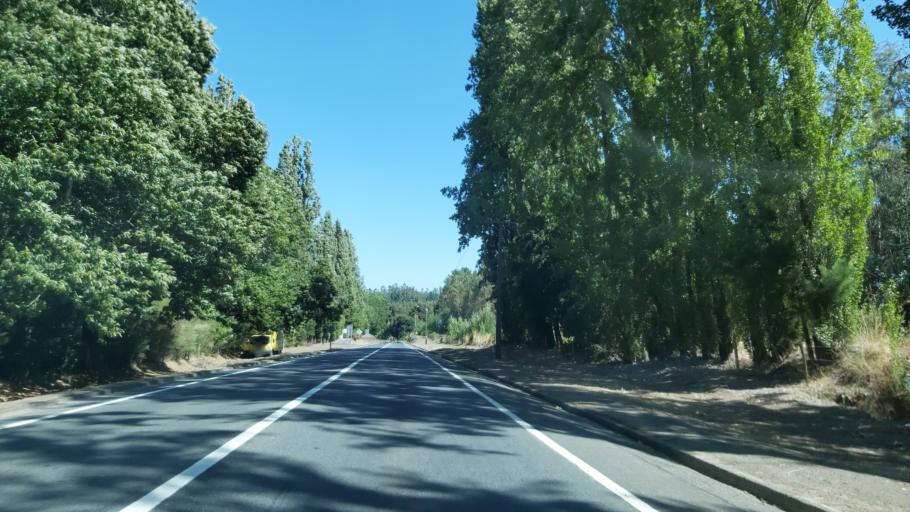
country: CL
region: Biobio
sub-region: Provincia de Concepcion
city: Coronel
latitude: -37.1080
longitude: -72.9885
